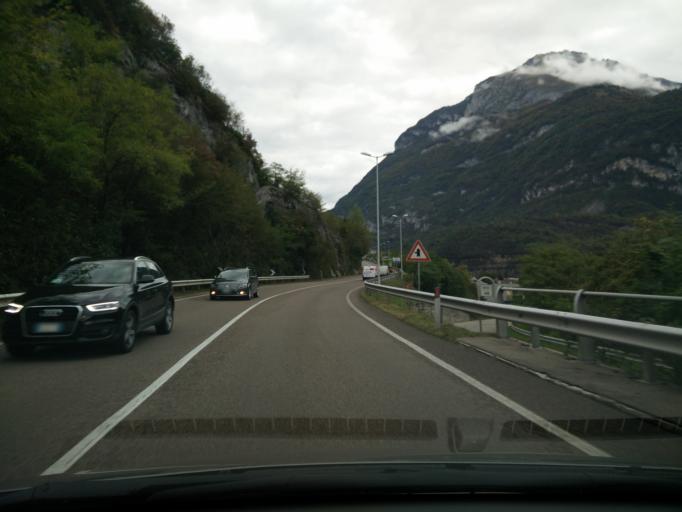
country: IT
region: Veneto
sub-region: Provincia di Belluno
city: Longarone
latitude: 46.2602
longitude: 12.3004
